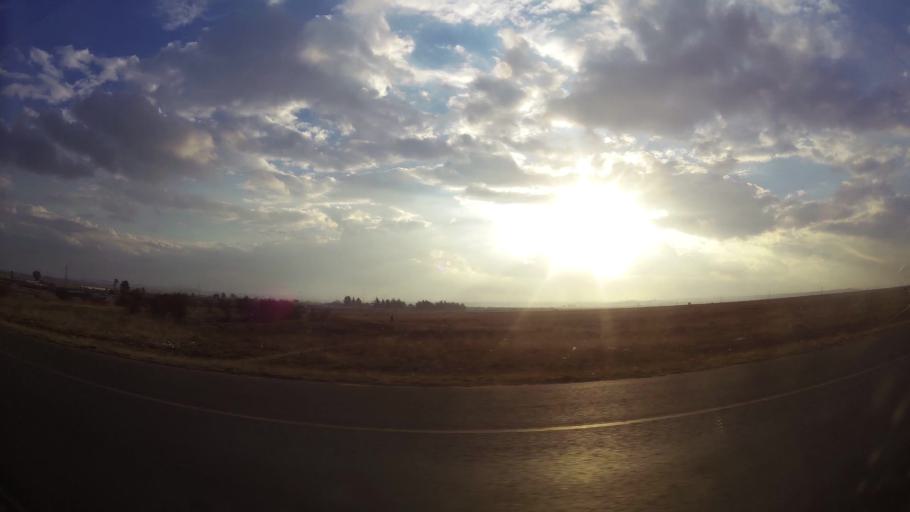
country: ZA
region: Gauteng
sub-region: Sedibeng District Municipality
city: Vanderbijlpark
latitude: -26.5995
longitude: 27.8188
